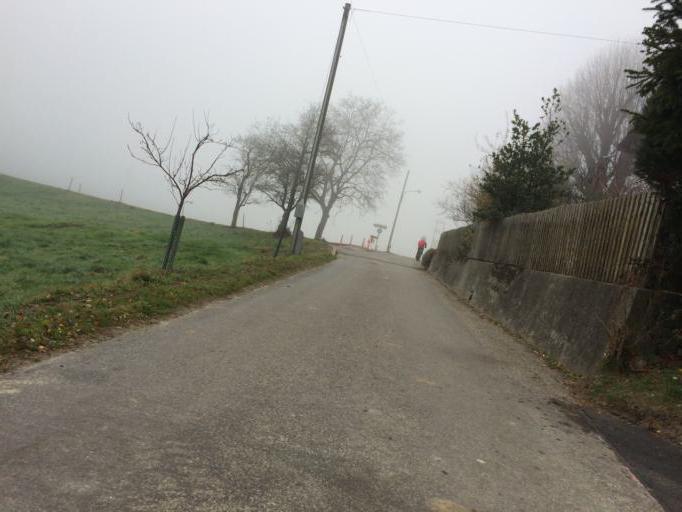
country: CH
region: Bern
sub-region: Bern-Mittelland District
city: Kehrsatz
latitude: 46.9082
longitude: 7.4499
